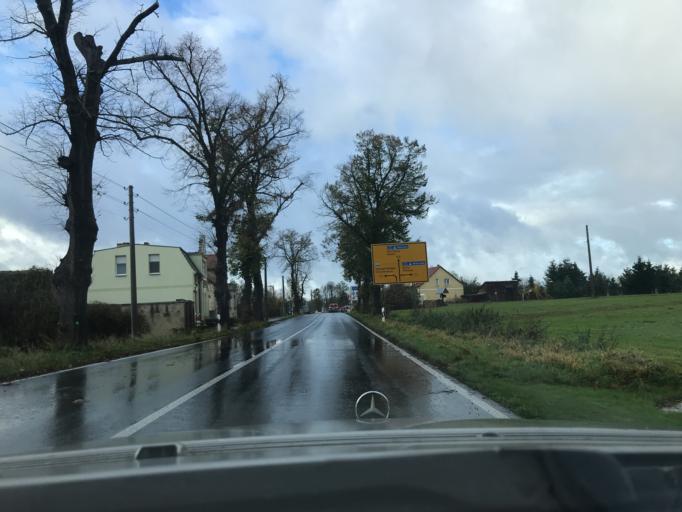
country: DE
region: Brandenburg
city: Beelitz
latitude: 52.2334
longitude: 12.9898
